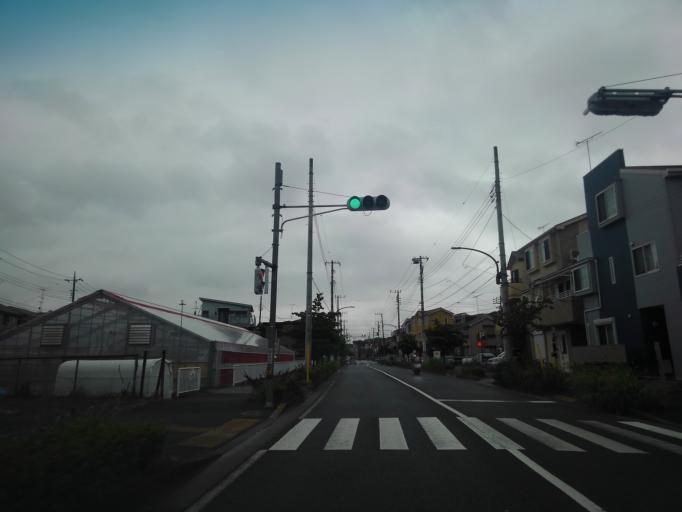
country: JP
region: Tokyo
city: Kokubunji
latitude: 35.6640
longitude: 139.4979
